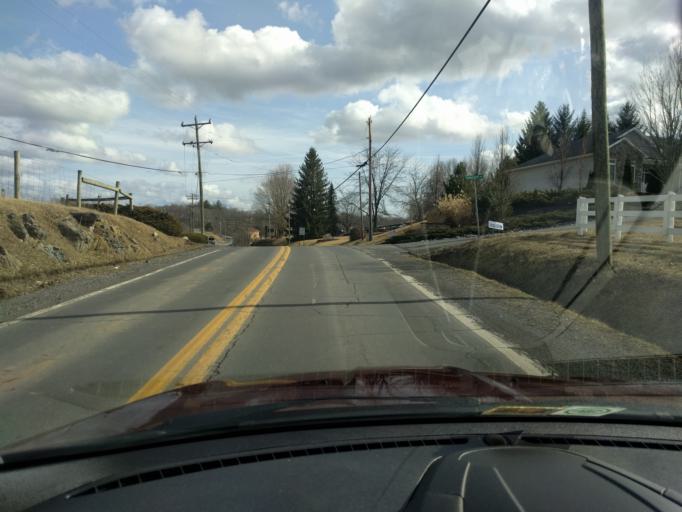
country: US
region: West Virginia
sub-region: Greenbrier County
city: Lewisburg
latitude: 37.8074
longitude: -80.4623
